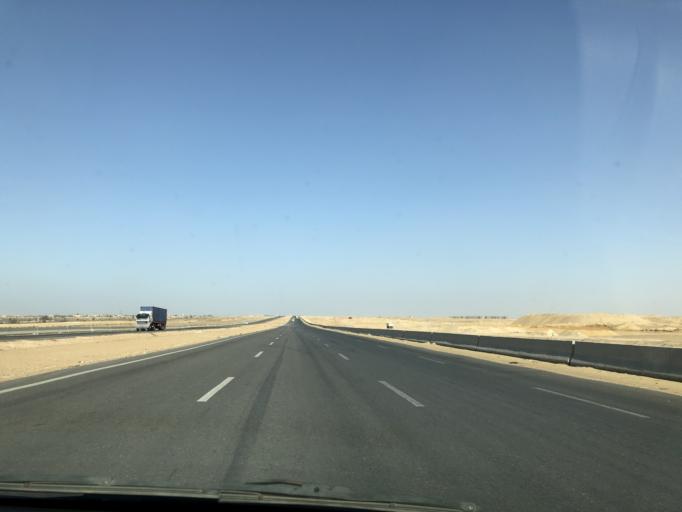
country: EG
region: Muhafazat al Minufiyah
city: Ashmun
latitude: 30.0674
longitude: 30.8534
